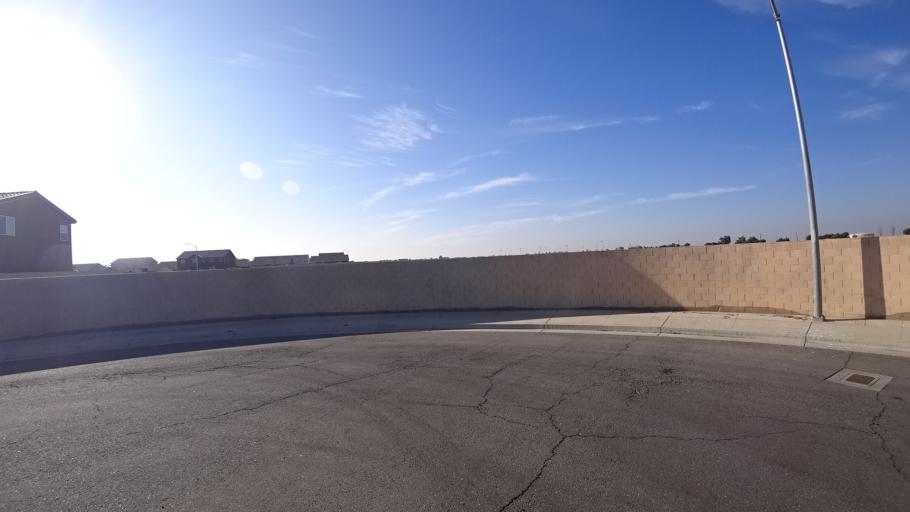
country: US
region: California
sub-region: Kern County
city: Greenfield
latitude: 35.2794
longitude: -119.0698
